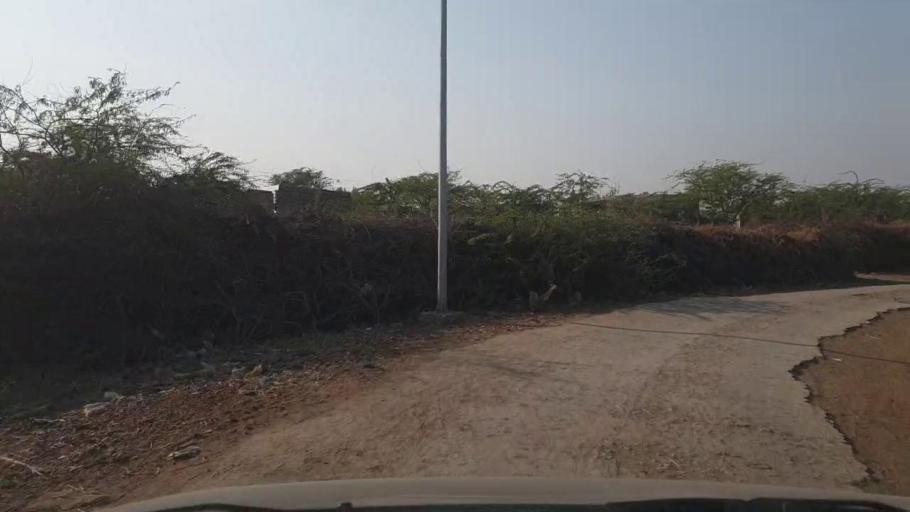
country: PK
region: Sindh
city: Digri
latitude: 25.2508
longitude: 69.1796
